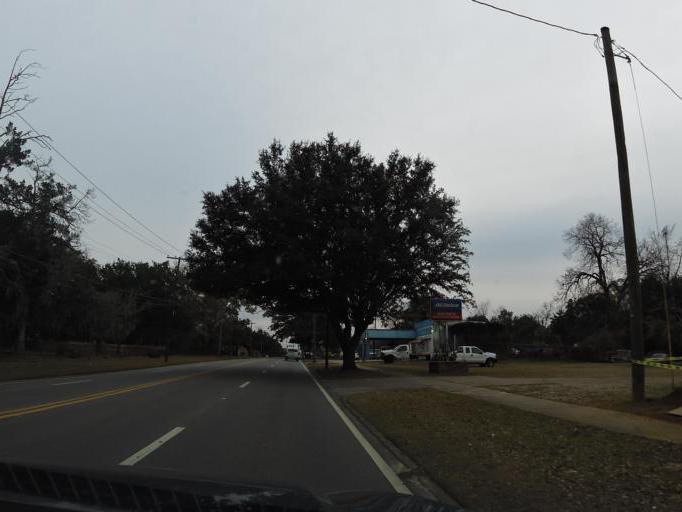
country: US
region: Georgia
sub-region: Thomas County
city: Thomasville
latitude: 30.8439
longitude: -83.9875
